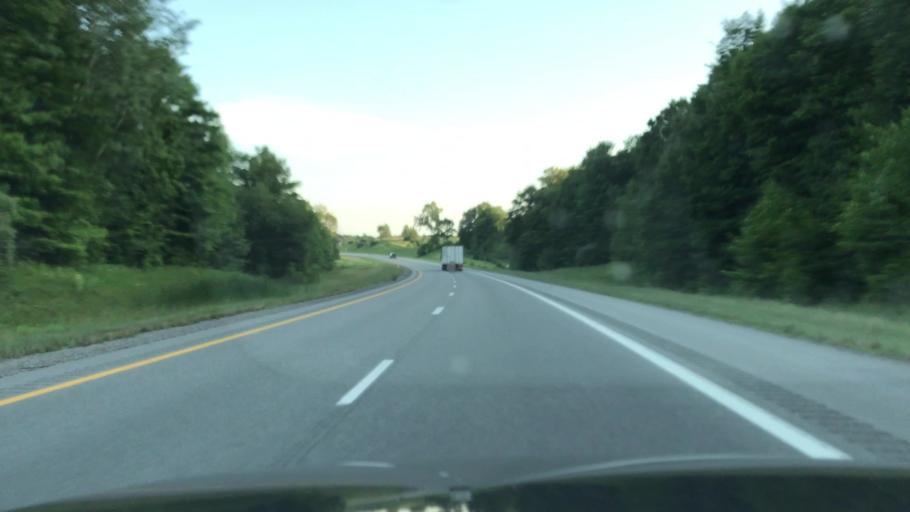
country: US
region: Michigan
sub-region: Osceola County
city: Reed City
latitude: 43.8667
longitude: -85.5346
